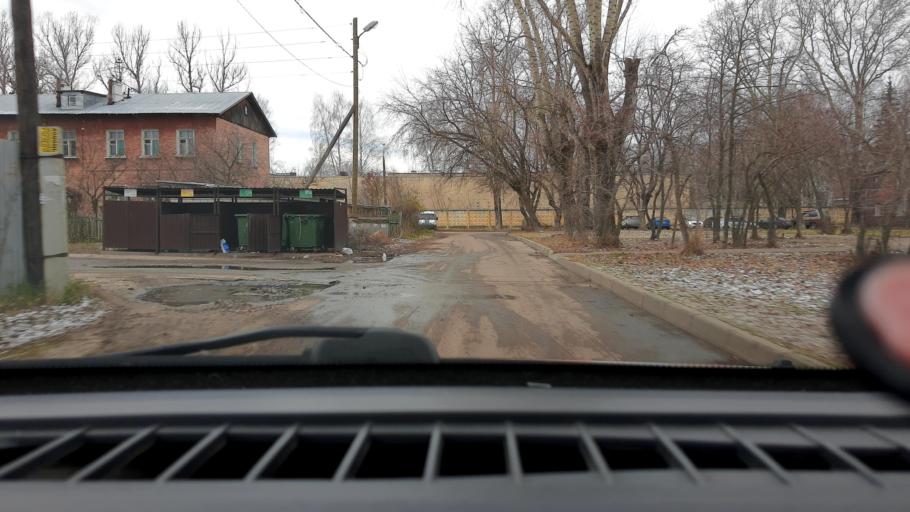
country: RU
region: Nizjnij Novgorod
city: Gorbatovka
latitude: 56.3814
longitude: 43.7843
